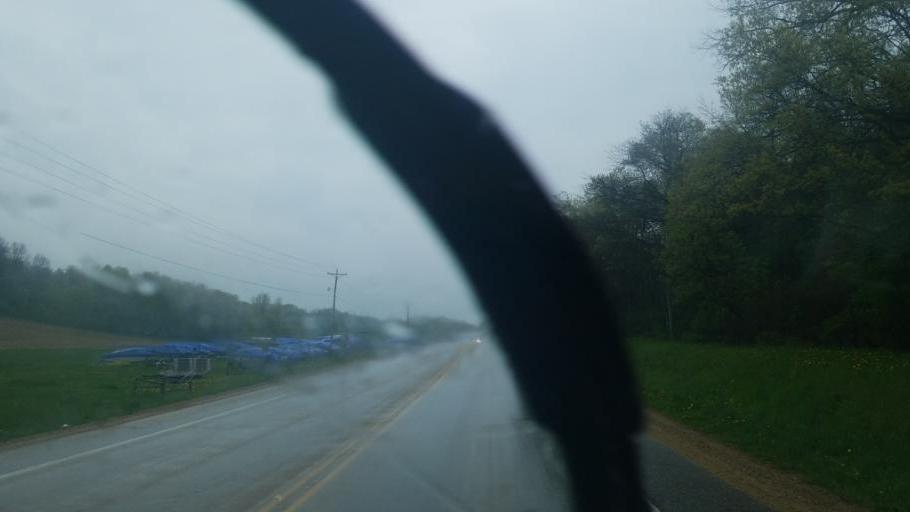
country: US
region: Wisconsin
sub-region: Sauk County
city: Reedsburg
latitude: 43.5889
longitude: -90.1261
